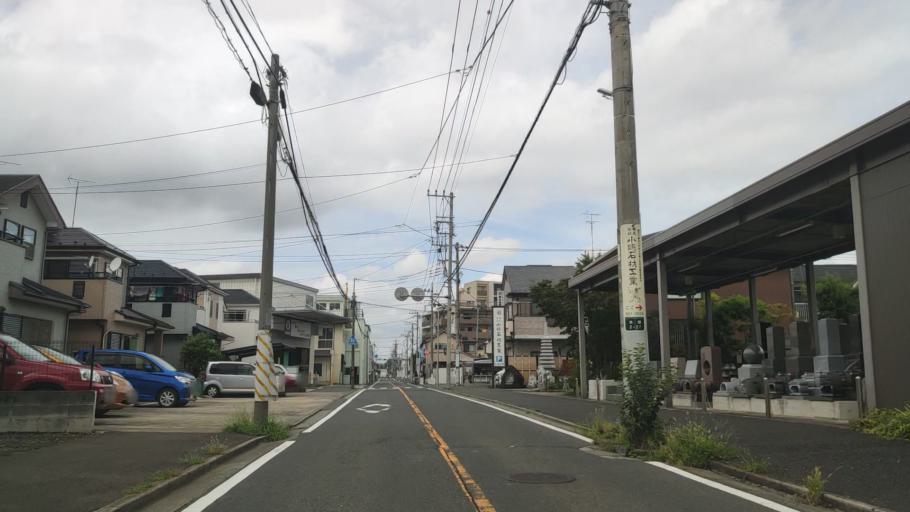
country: JP
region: Kanagawa
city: Minami-rinkan
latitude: 35.4768
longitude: 139.4757
